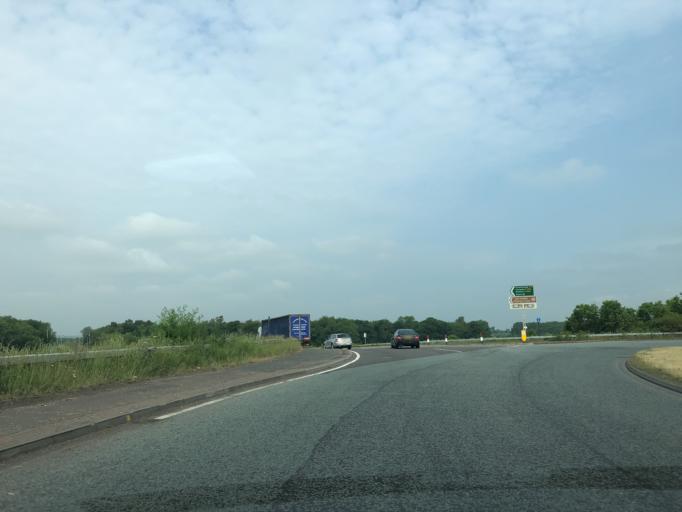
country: GB
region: England
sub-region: City and Borough of Leeds
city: Wetherby
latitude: 54.0089
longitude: -1.3786
